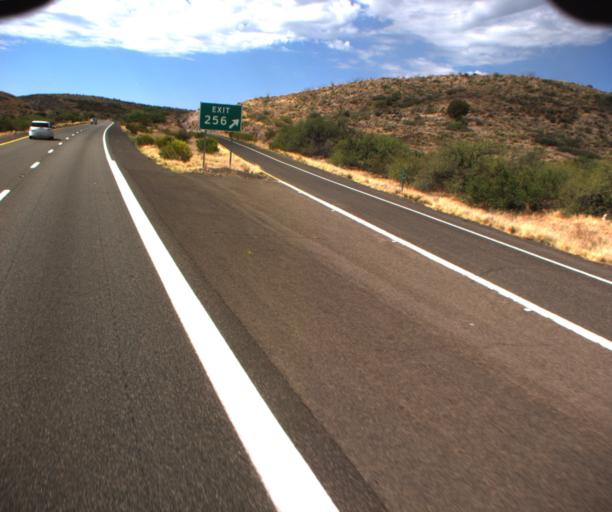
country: US
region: Arizona
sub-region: Yavapai County
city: Cordes Lakes
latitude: 34.2393
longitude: -112.1151
